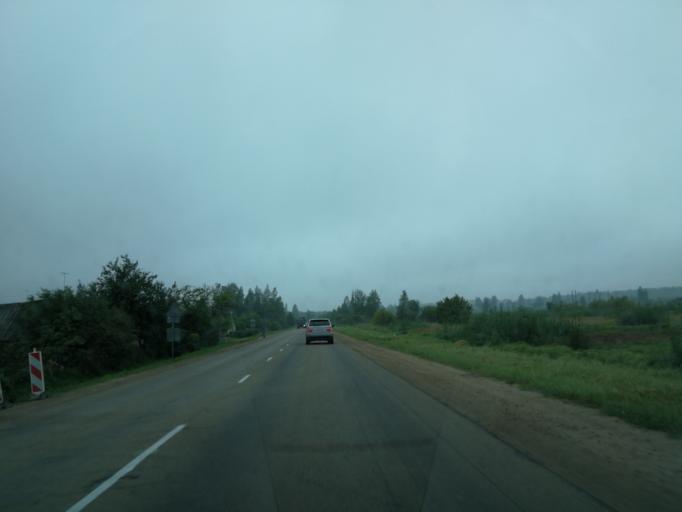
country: LV
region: Preilu Rajons
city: Preili
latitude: 56.3001
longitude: 26.7292
